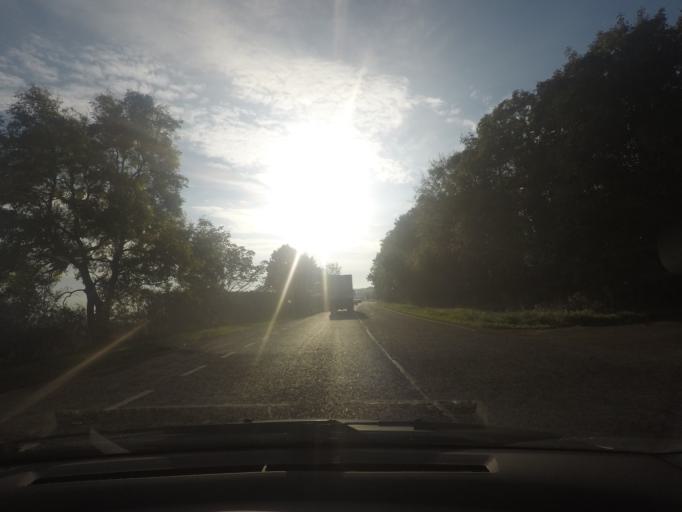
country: GB
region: England
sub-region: East Riding of Yorkshire
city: Hayton
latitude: 53.8926
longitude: -0.7372
